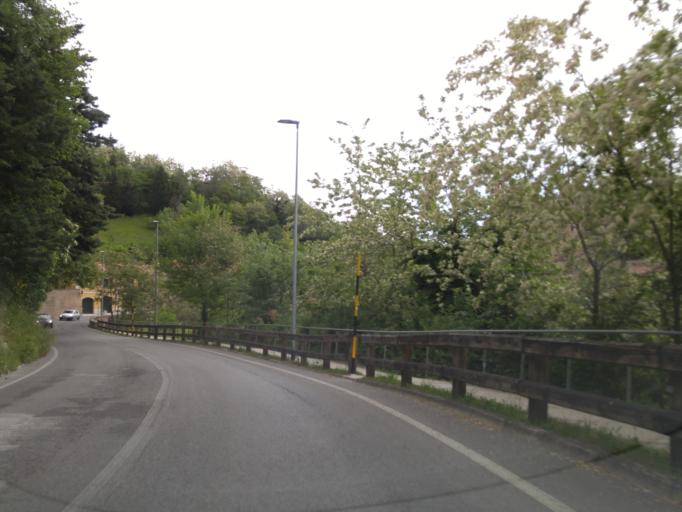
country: IT
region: The Marches
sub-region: Provincia di Pesaro e Urbino
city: Urbino
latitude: 43.7221
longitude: 12.6322
